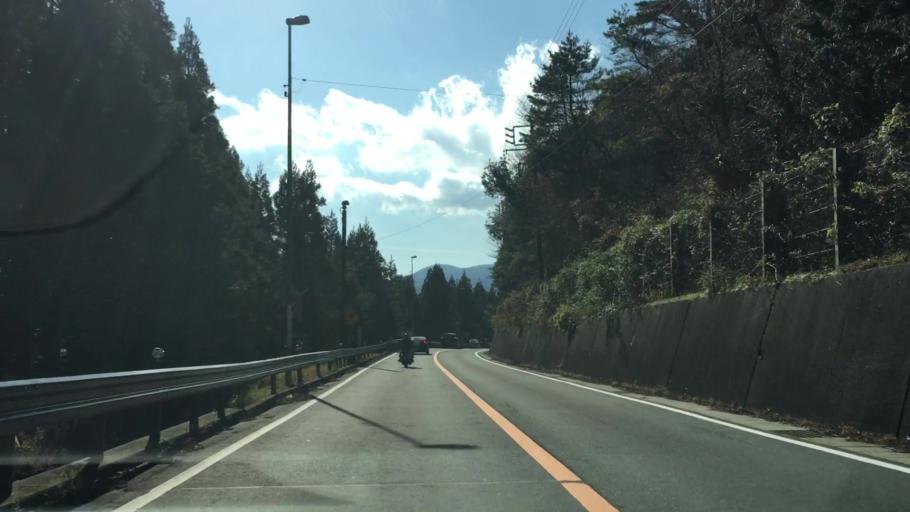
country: JP
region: Shizuoka
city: Gotemba
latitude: 35.3853
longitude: 138.8591
